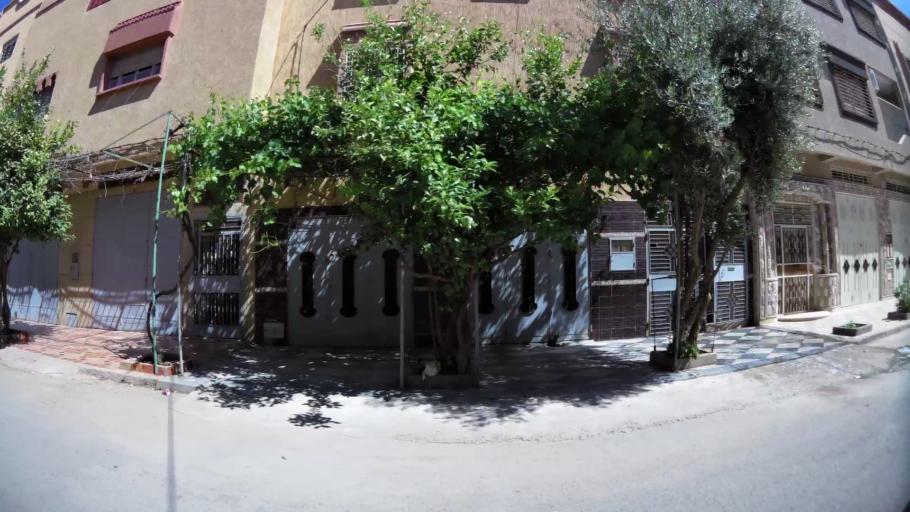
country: MA
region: Oriental
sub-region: Oujda-Angad
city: Oujda
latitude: 34.6693
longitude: -1.9278
